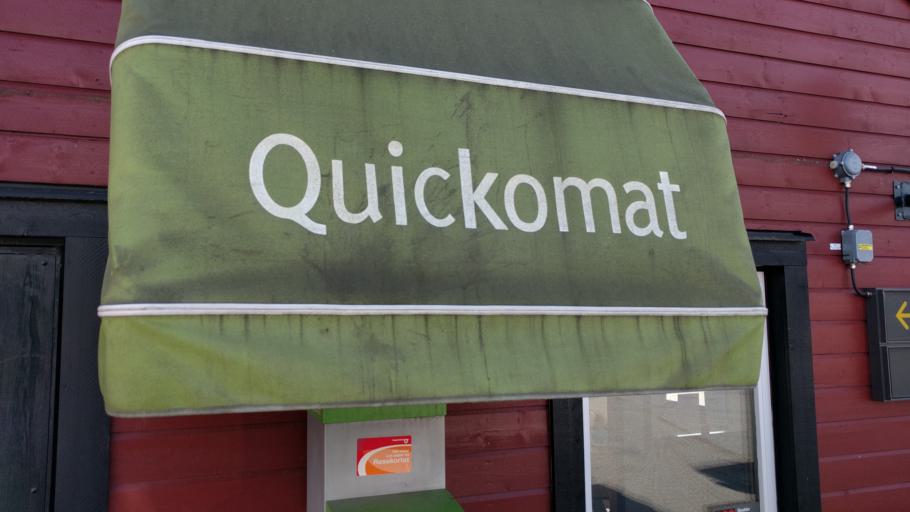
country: SE
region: OEstergoetland
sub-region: Kinda Kommun
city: Kisa
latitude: 57.9858
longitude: 15.6333
